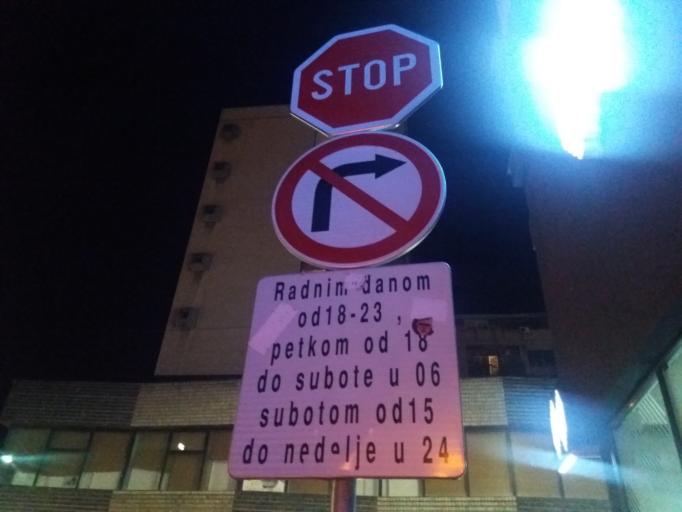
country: RS
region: Central Serbia
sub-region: Zlatiborski Okrug
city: Uzice
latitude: 43.8562
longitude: 19.8391
